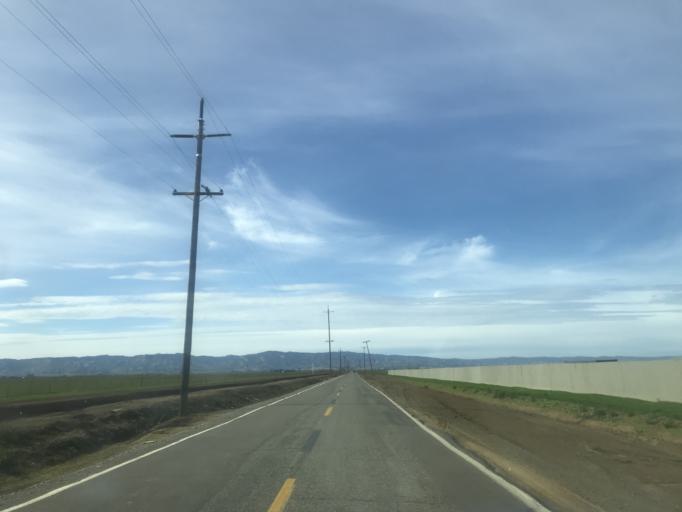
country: US
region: California
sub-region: Yolo County
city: Cottonwood
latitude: 38.6637
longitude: -121.9063
